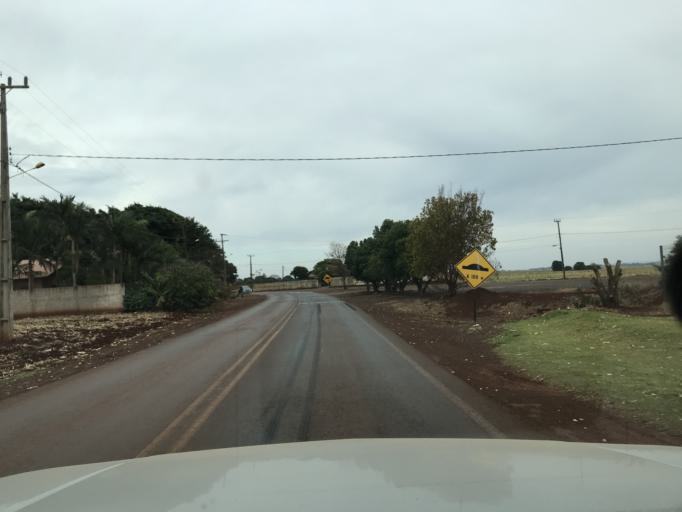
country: BR
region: Parana
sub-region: Palotina
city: Palotina
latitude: -24.4188
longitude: -53.8804
